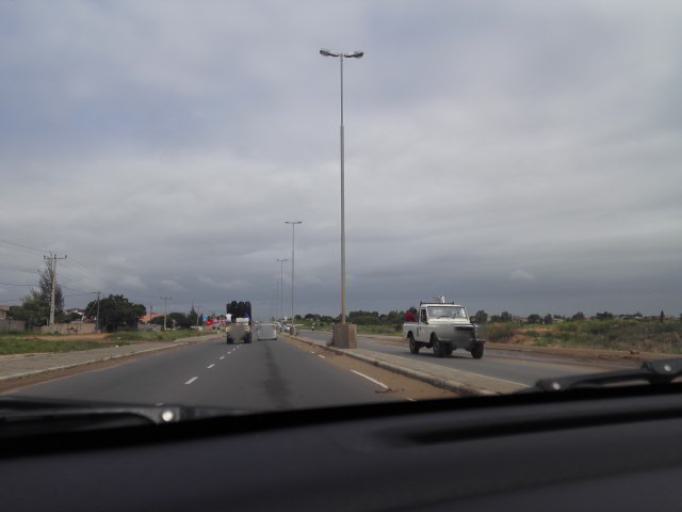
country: MZ
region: Maputo City
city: Maputo
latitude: -25.8276
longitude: 32.6055
